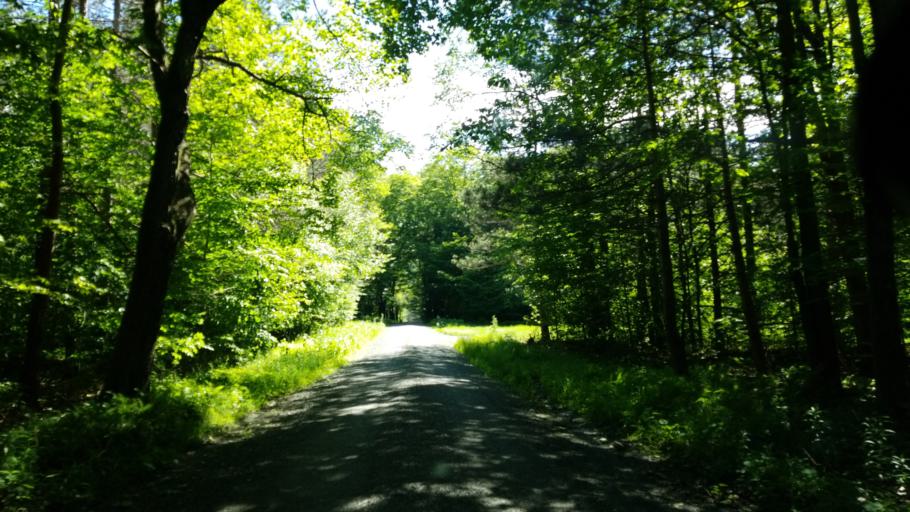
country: US
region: Pennsylvania
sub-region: Clearfield County
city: Clearfield
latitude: 41.2063
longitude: -78.4188
